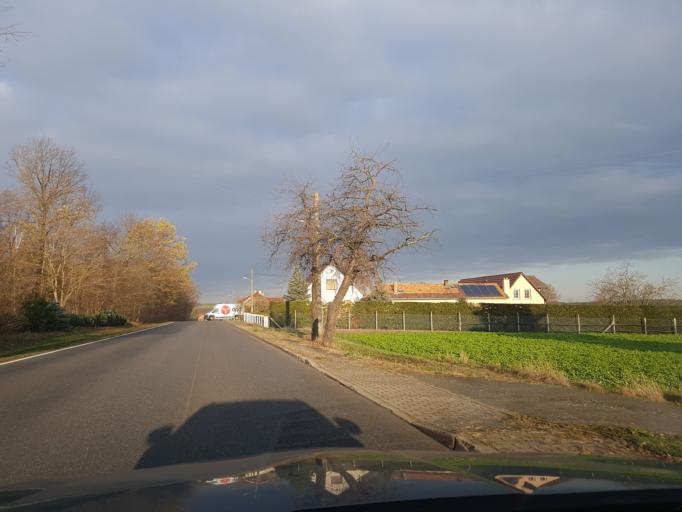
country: DE
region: Brandenburg
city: Kasel-Golzig
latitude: 51.8966
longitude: 13.6821
